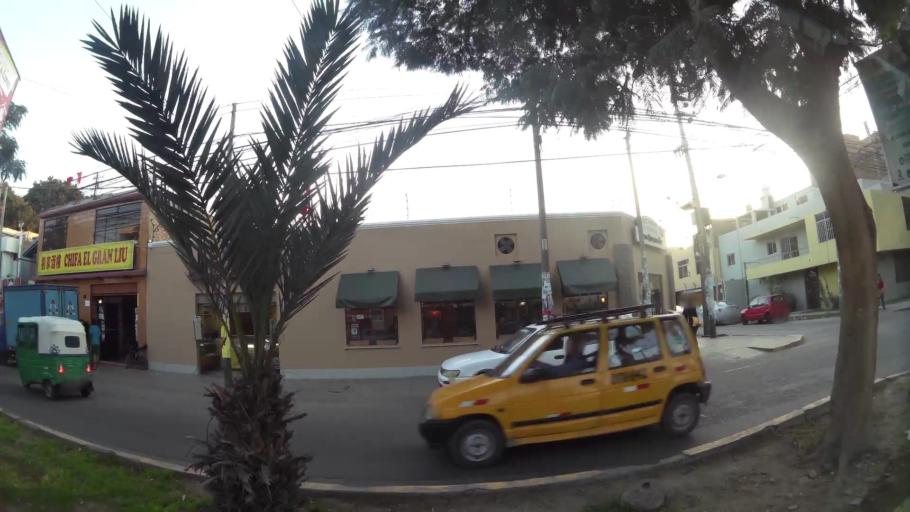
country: PE
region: Ica
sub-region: Provincia de Ica
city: Ica
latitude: -14.0740
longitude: -75.7274
